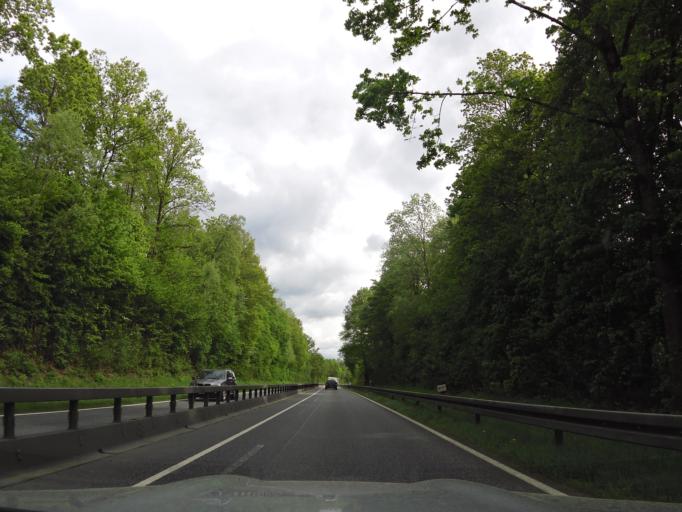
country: DE
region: Hesse
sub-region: Regierungsbezirk Giessen
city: Lohnberg
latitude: 50.5215
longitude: 8.2753
